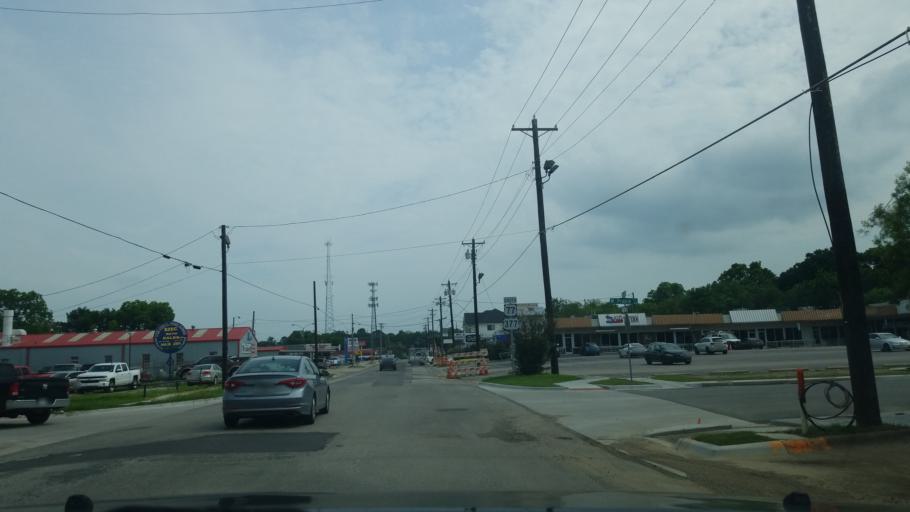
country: US
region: Texas
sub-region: Denton County
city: Denton
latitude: 33.2109
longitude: -97.1338
